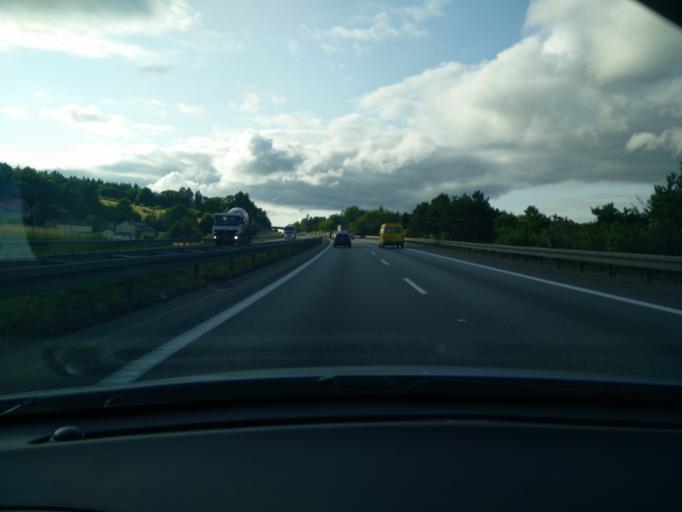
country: PL
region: Pomeranian Voivodeship
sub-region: Gdynia
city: Wielki Kack
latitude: 54.4606
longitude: 18.4874
